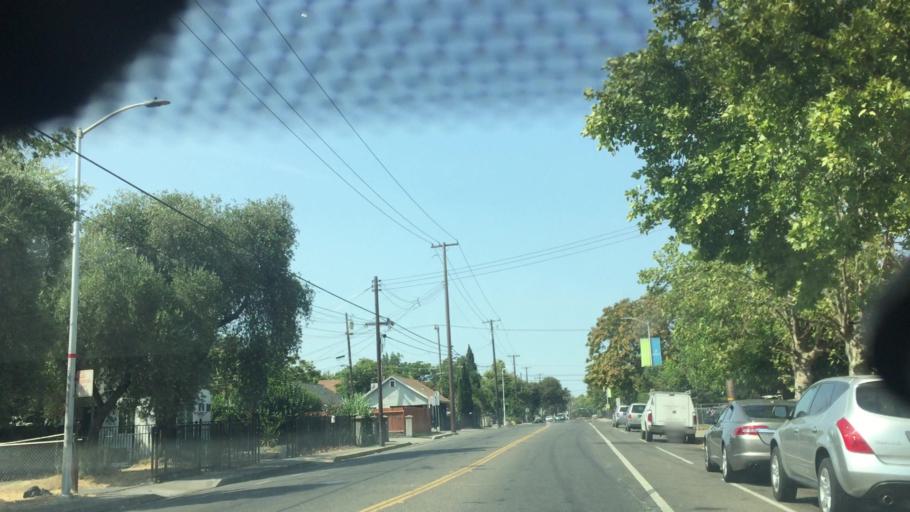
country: US
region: California
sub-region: Sacramento County
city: Parkway
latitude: 38.5399
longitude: -121.4647
